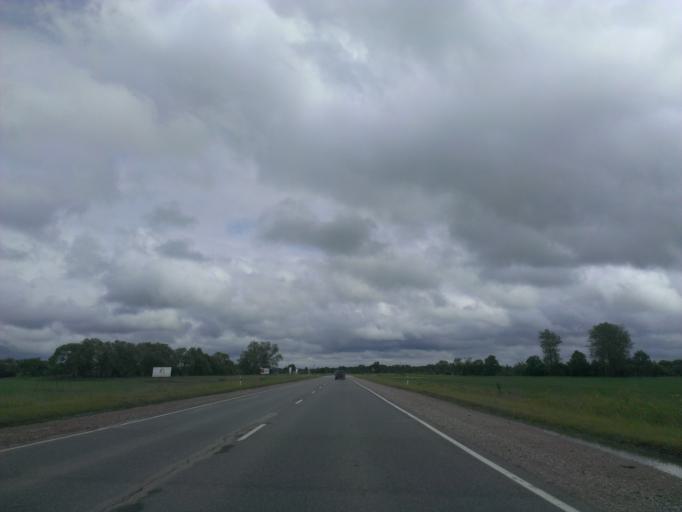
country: LV
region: Grobina
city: Grobina
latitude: 56.5335
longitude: 21.1241
